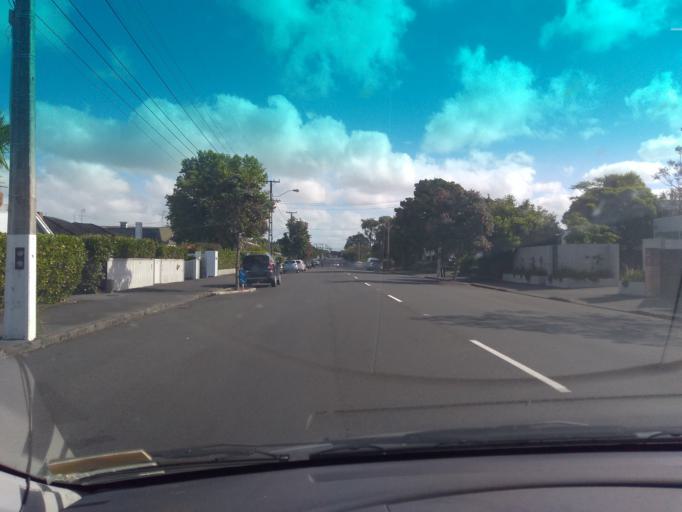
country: NZ
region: Auckland
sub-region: Auckland
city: Rosebank
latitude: -36.8552
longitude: 174.7040
